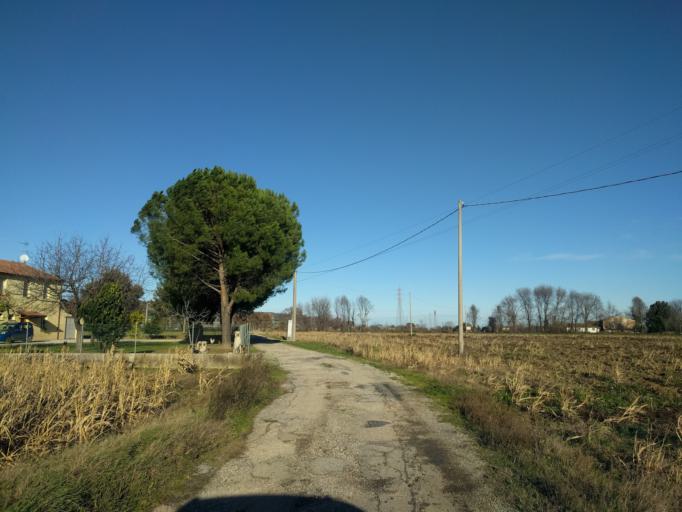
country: IT
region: The Marches
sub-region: Provincia di Pesaro e Urbino
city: Cuccurano
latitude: 43.7816
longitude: 12.9515
